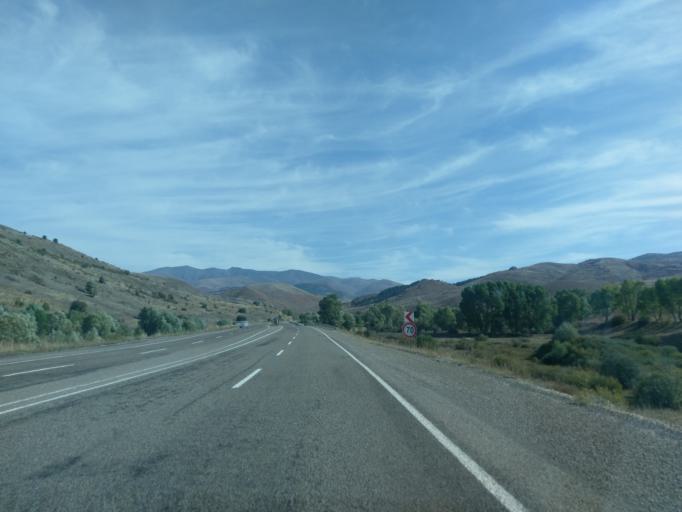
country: TR
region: Sivas
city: Imranli
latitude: 39.8400
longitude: 38.2831
